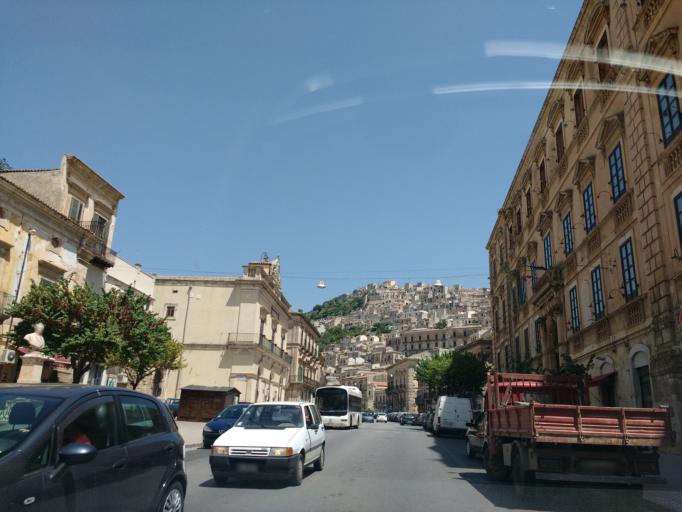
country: IT
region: Sicily
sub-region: Ragusa
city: Modica
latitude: 36.8618
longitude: 14.7599
